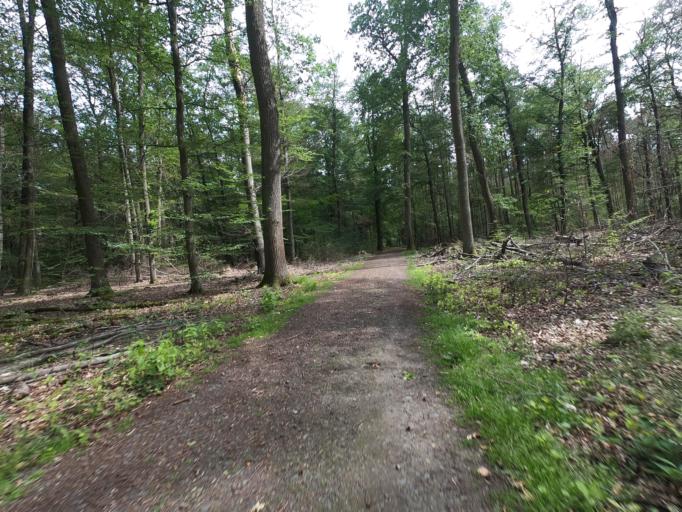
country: DE
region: Hesse
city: Heusenstamm
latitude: 50.0609
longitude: 8.7653
